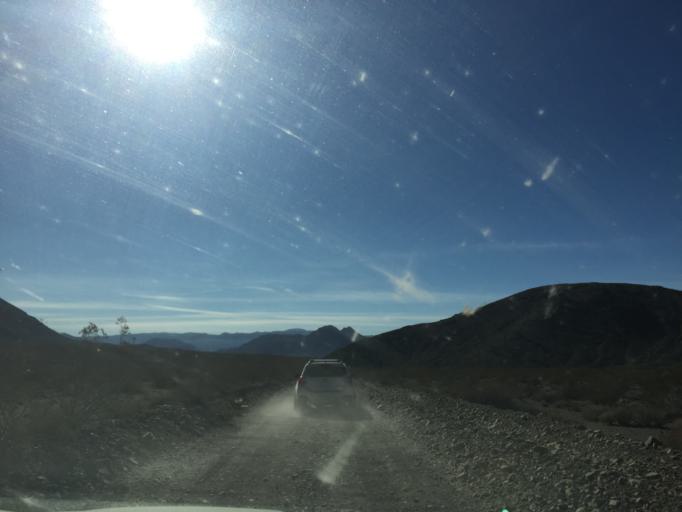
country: US
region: California
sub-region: Inyo County
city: Lone Pine
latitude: 36.7668
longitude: -117.5358
